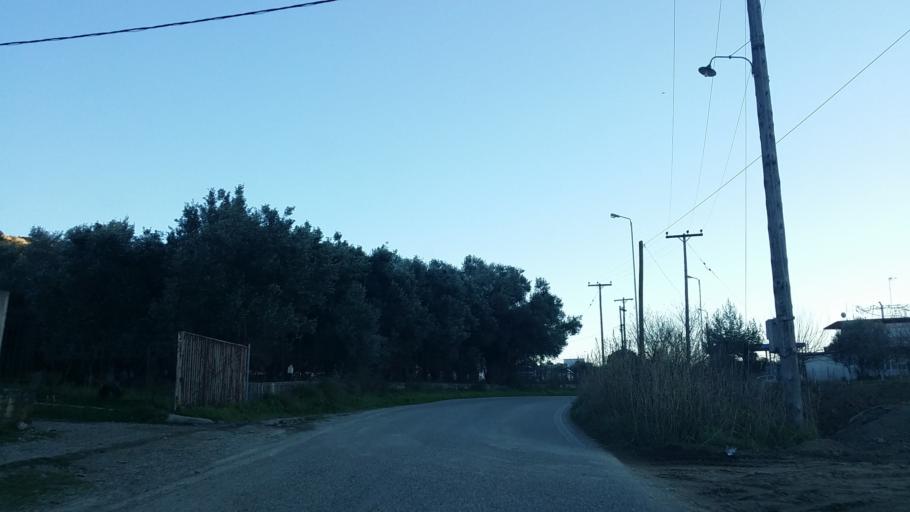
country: GR
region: West Greece
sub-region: Nomos Aitolias kai Akarnanias
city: Neapolis
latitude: 38.6995
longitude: 21.3530
